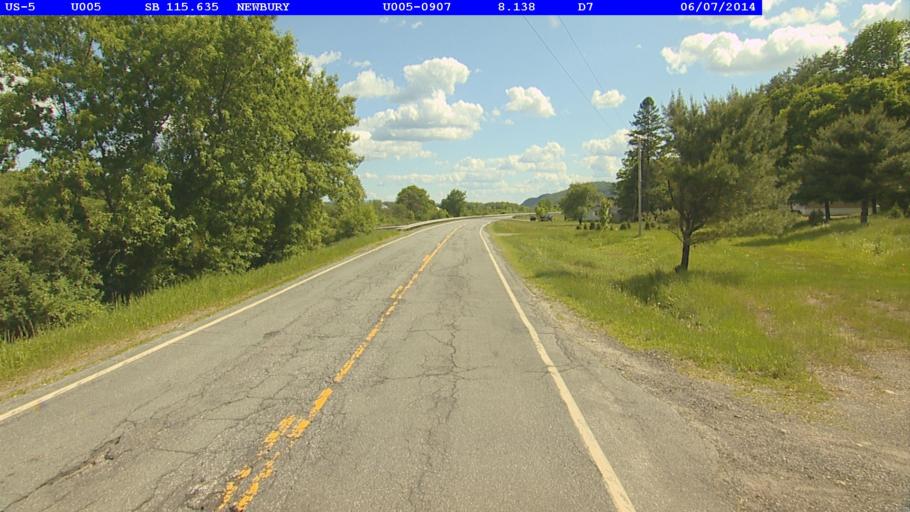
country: US
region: New Hampshire
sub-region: Grafton County
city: Woodsville
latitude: 44.1352
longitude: -72.0430
